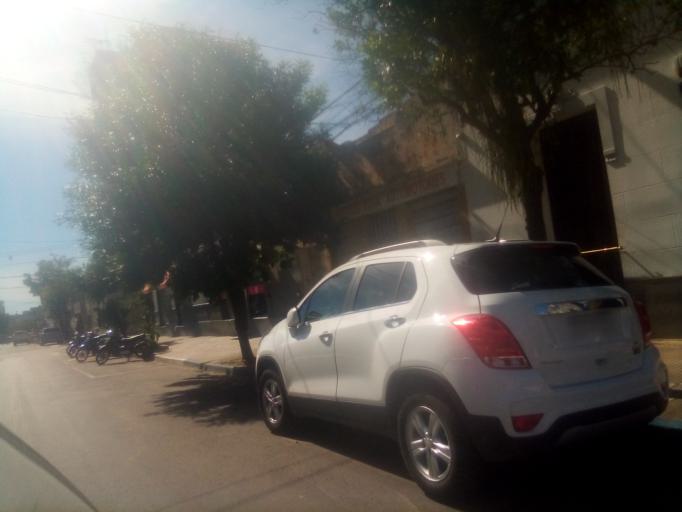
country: AR
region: Corrientes
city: Corrientes
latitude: -27.4703
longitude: -58.8316
